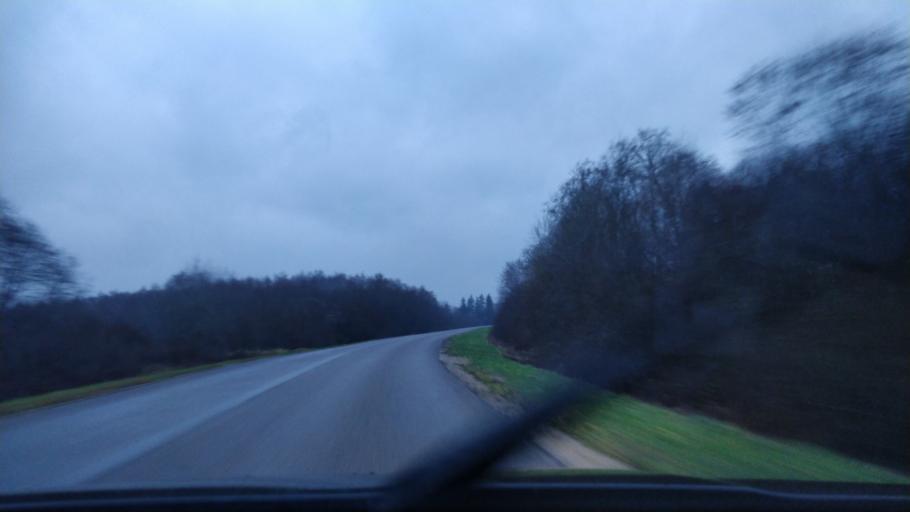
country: EE
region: Laeaene
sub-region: Lihula vald
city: Lihula
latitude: 58.7038
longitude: 23.8612
